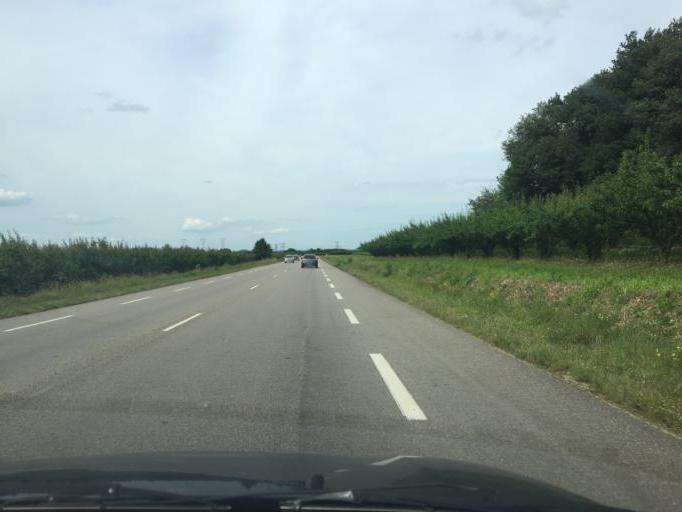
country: FR
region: Rhone-Alpes
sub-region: Departement de la Drome
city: Beaumont-Monteux
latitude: 44.9939
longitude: 4.9131
